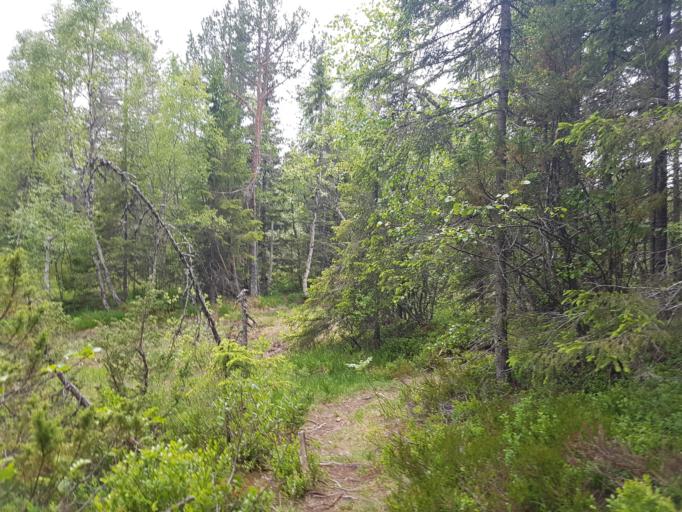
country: NO
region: Sor-Trondelag
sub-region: Trondheim
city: Trondheim
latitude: 63.4105
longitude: 10.3241
